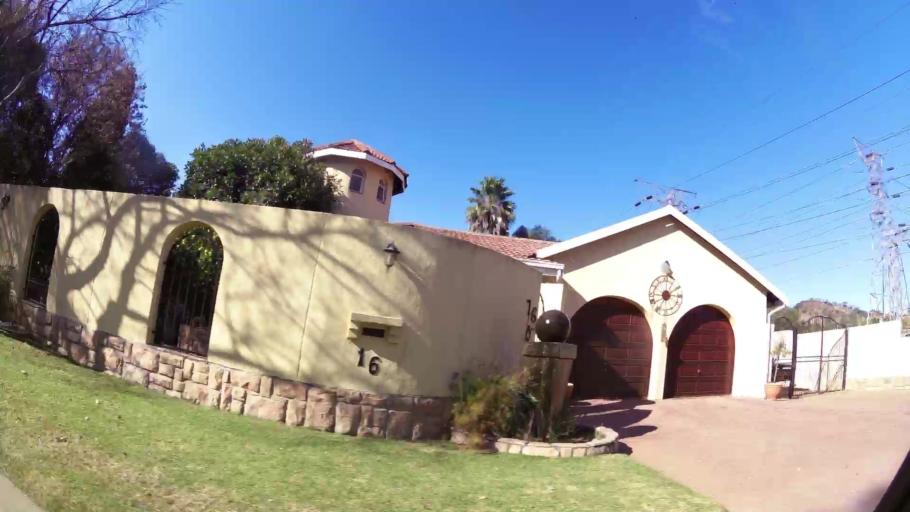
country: ZA
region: Gauteng
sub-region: City of Johannesburg Metropolitan Municipality
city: Johannesburg
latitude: -26.2759
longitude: 28.0238
